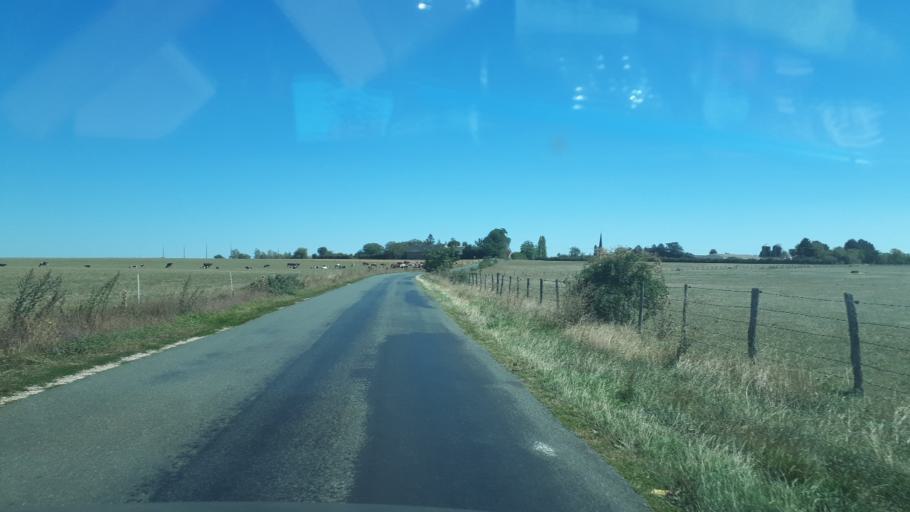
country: FR
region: Centre
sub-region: Departement du Cher
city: Rians
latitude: 47.1850
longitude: 2.6986
